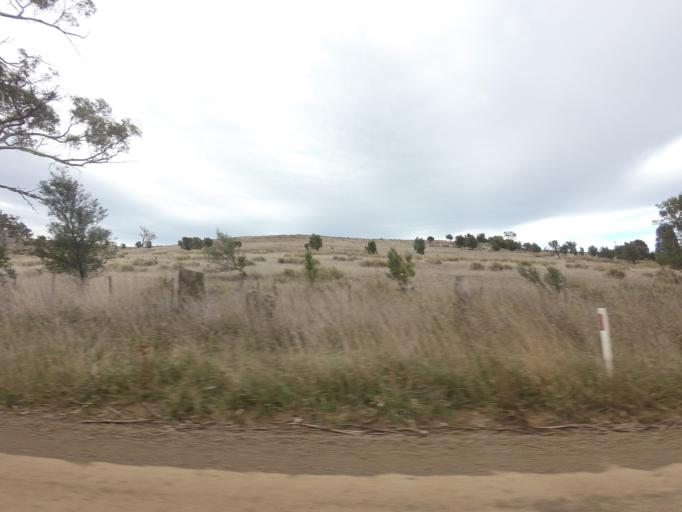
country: AU
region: Tasmania
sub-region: Derwent Valley
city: New Norfolk
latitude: -42.5533
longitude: 146.9048
